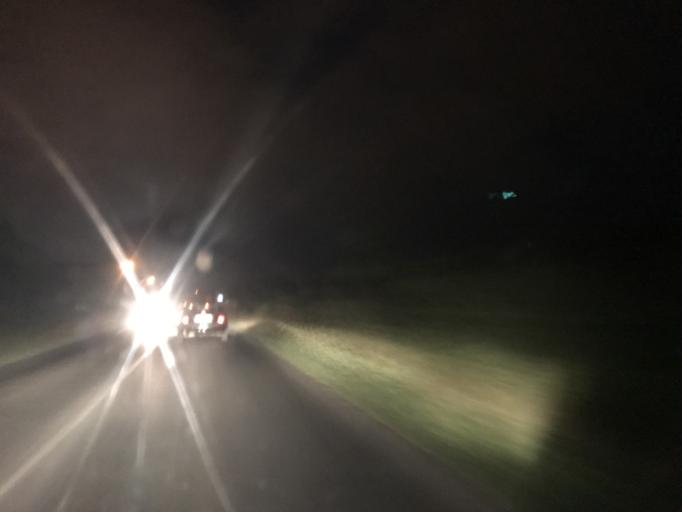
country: RS
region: Central Serbia
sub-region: Belgrade
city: Zvezdara
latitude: 44.7557
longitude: 20.5771
